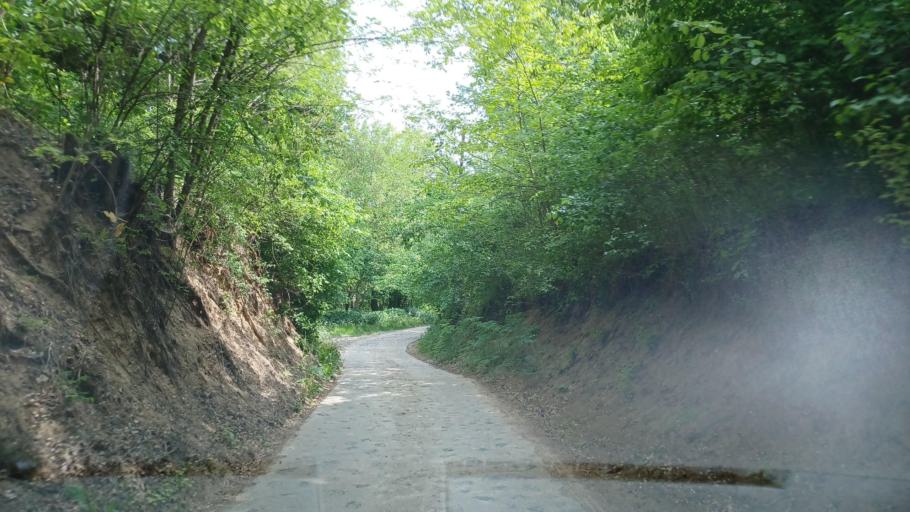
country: HU
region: Baranya
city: Kozarmisleny
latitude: 45.9716
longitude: 18.3575
